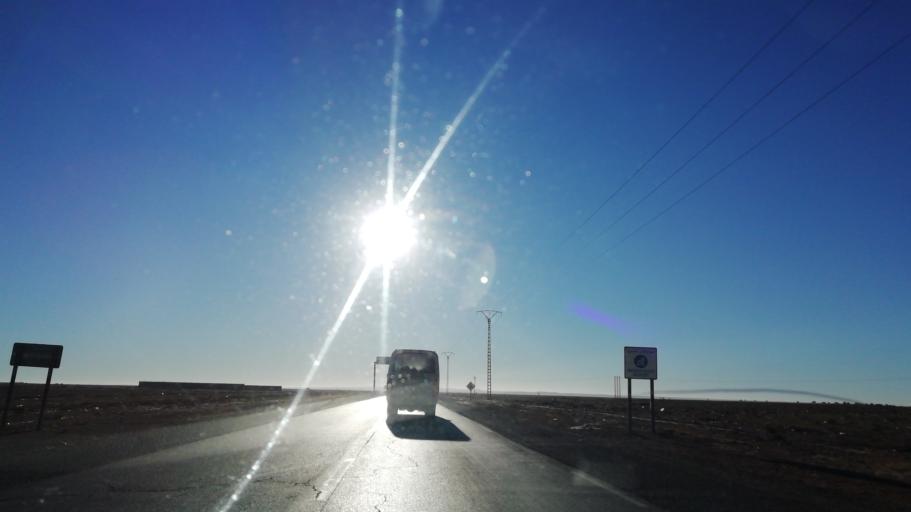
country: DZ
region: Saida
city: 'Ain el Hadjar
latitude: 34.0213
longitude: 0.1034
